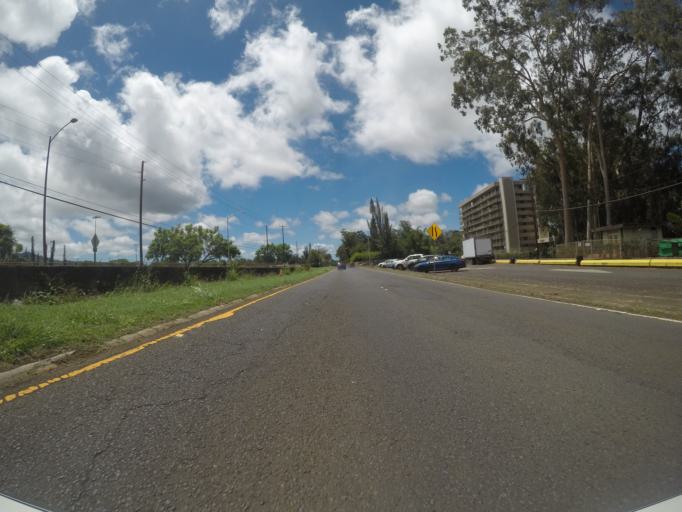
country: US
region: Hawaii
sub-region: Honolulu County
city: Schofield Barracks
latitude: 21.4953
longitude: -158.0506
